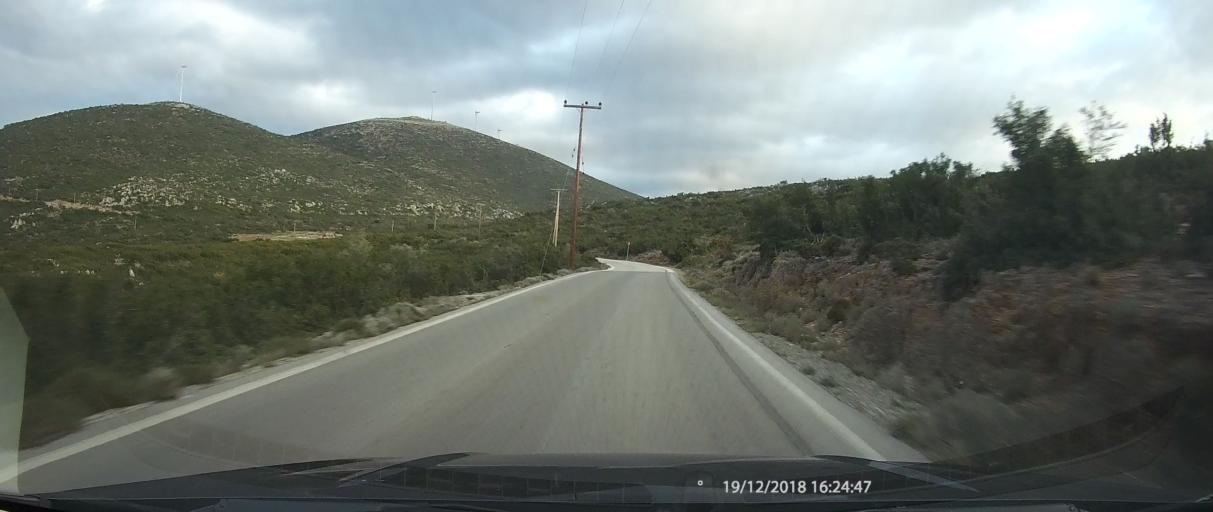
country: GR
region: Peloponnese
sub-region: Nomos Lakonias
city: Kato Glikovrisi
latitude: 36.9536
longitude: 22.8426
